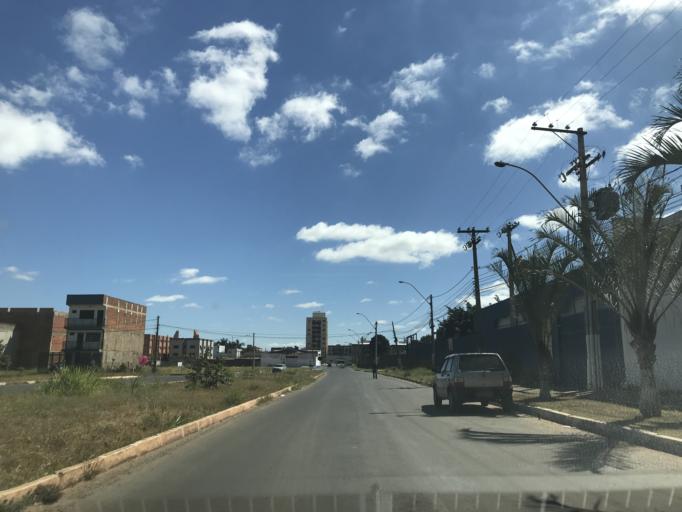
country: BR
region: Federal District
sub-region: Brasilia
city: Brasilia
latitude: -15.8724
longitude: -48.0258
